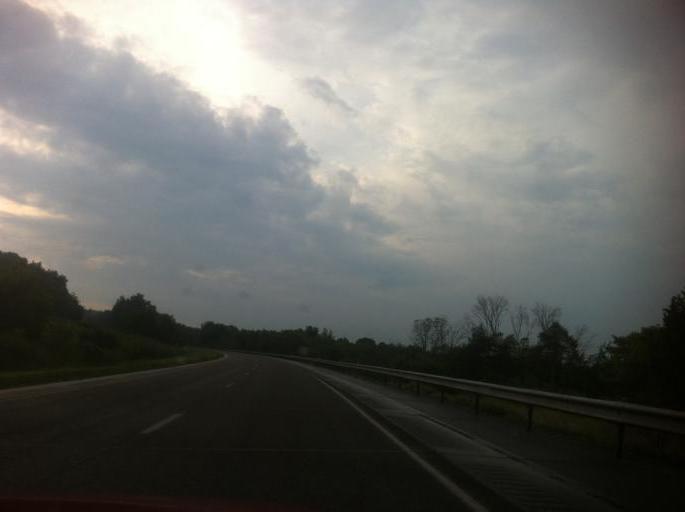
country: US
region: Pennsylvania
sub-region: Clarion County
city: Knox
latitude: 41.1957
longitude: -79.6199
